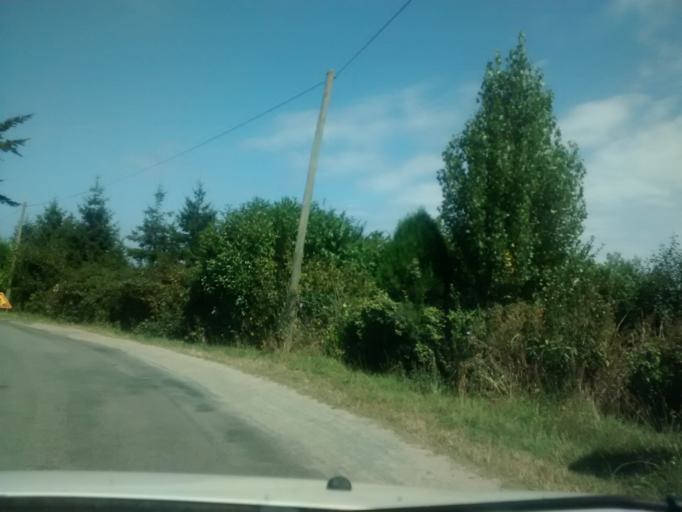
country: FR
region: Brittany
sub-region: Departement d'Ille-et-Vilaine
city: Cancale
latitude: 48.6923
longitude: -1.8816
